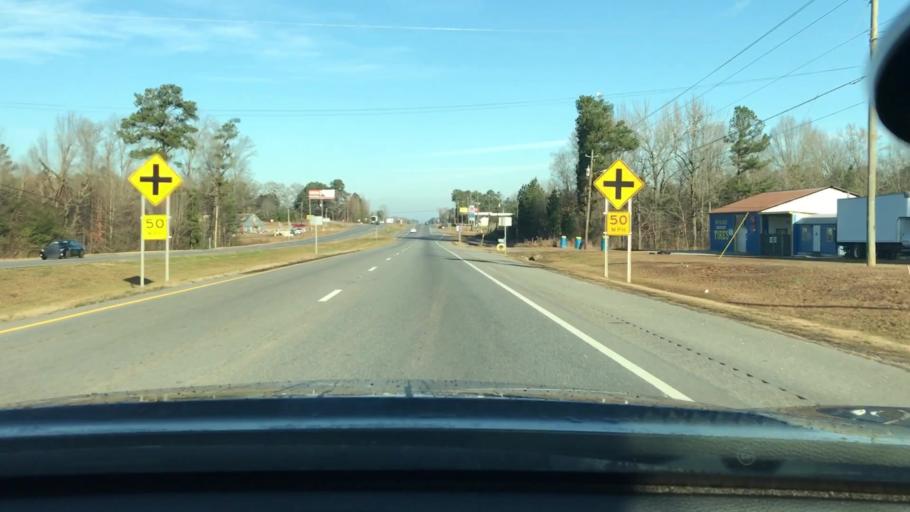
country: US
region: Alabama
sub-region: Talladega County
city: Mignon
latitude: 33.2194
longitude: -86.3183
